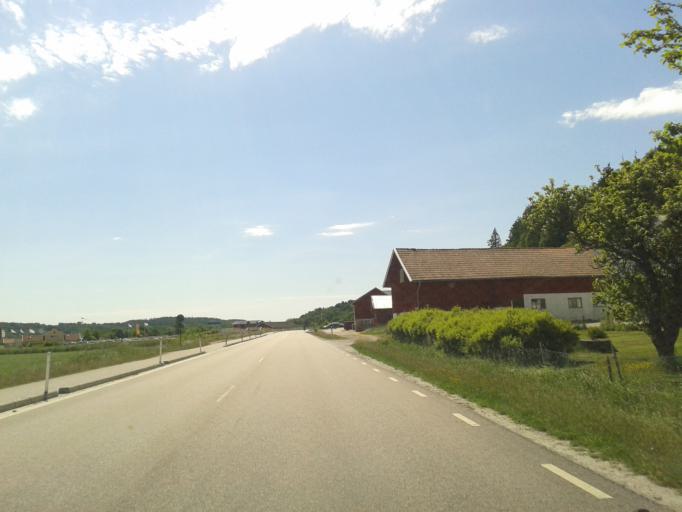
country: SE
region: Vaestra Goetaland
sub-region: Stenungsunds Kommun
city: Stora Hoga
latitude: 58.0296
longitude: 11.8719
